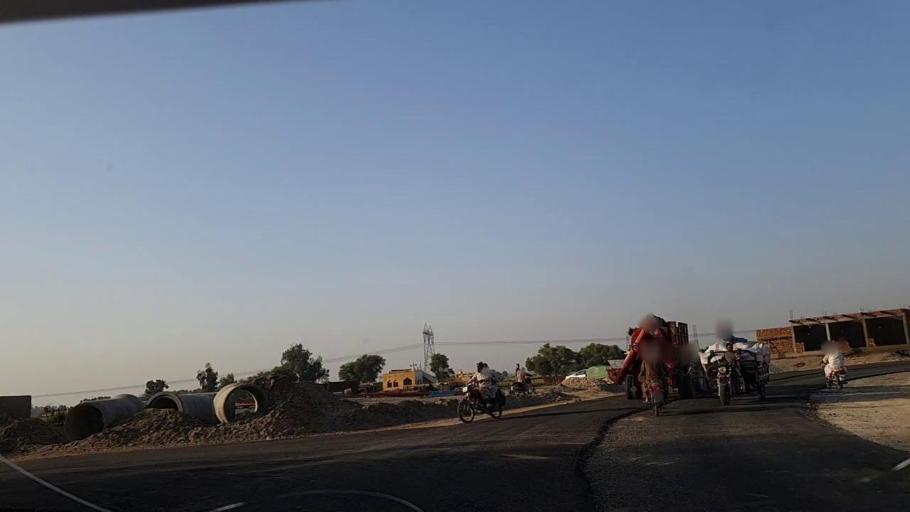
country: PK
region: Sindh
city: Rustam jo Goth
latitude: 27.9660
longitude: 68.7998
